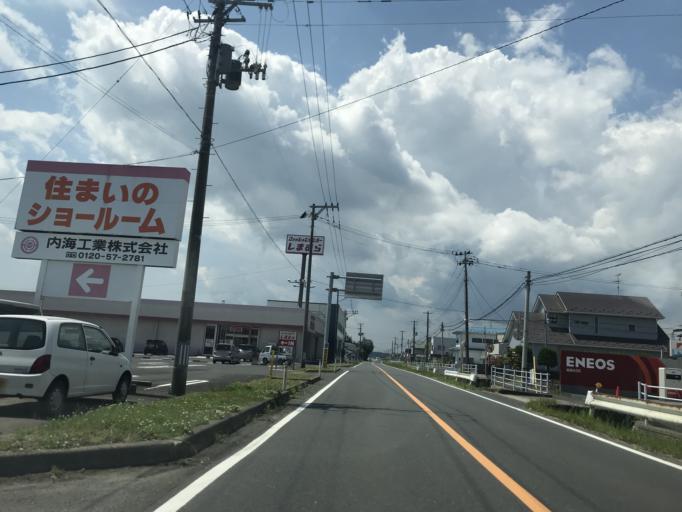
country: JP
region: Miyagi
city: Wakuya
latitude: 38.4632
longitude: 141.0904
